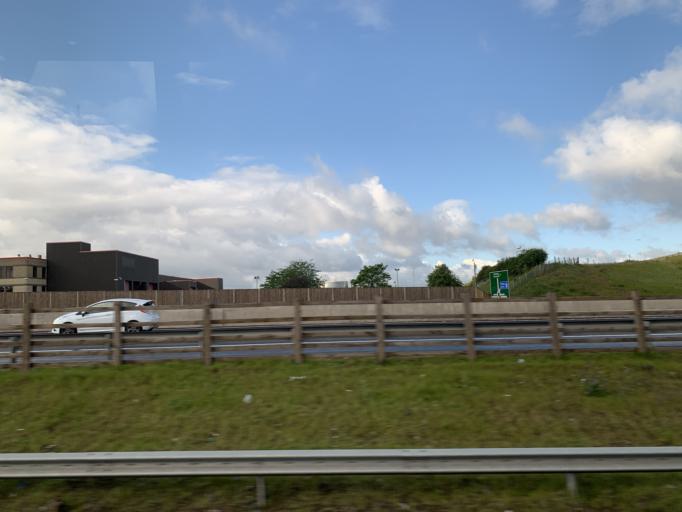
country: GB
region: Scotland
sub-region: North Lanarkshire
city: Chapelhall
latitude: 55.8333
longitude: -3.9588
